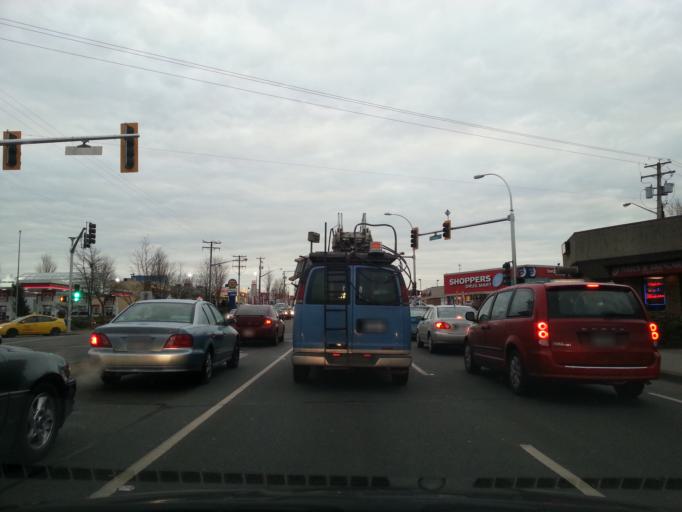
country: CA
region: British Columbia
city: Surrey
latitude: 49.1662
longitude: -122.8019
